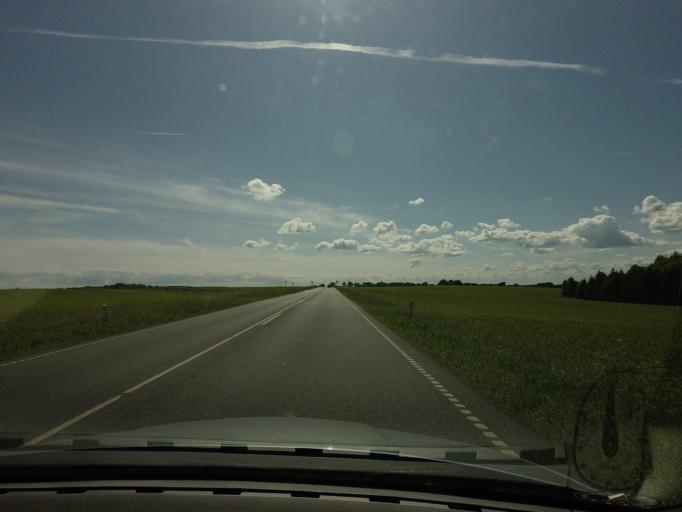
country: DK
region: Central Jutland
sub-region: Syddjurs Kommune
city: Ebeltoft
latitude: 56.3383
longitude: 10.7421
